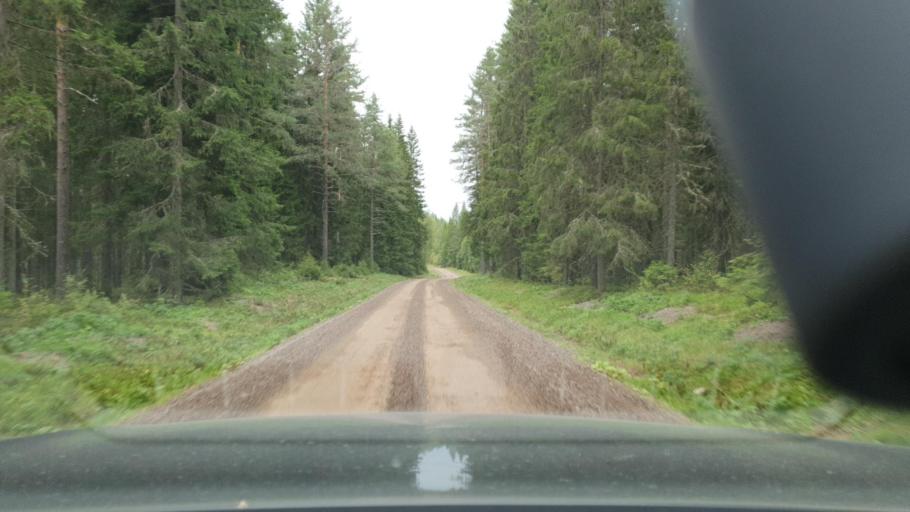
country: SE
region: Vaermland
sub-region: Arvika Kommun
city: Arvika
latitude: 59.9813
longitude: 12.6597
